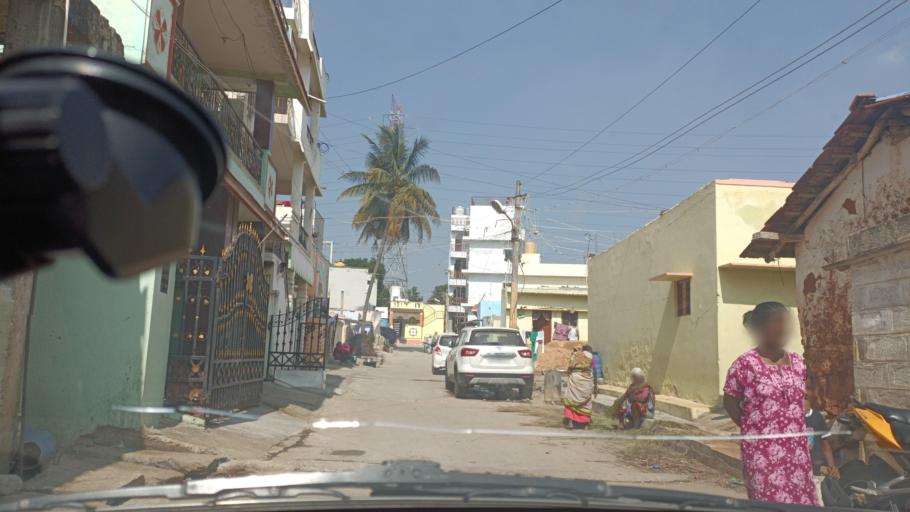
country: IN
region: Karnataka
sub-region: Bangalore Rural
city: Devanhalli
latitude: 13.1831
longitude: 77.6429
